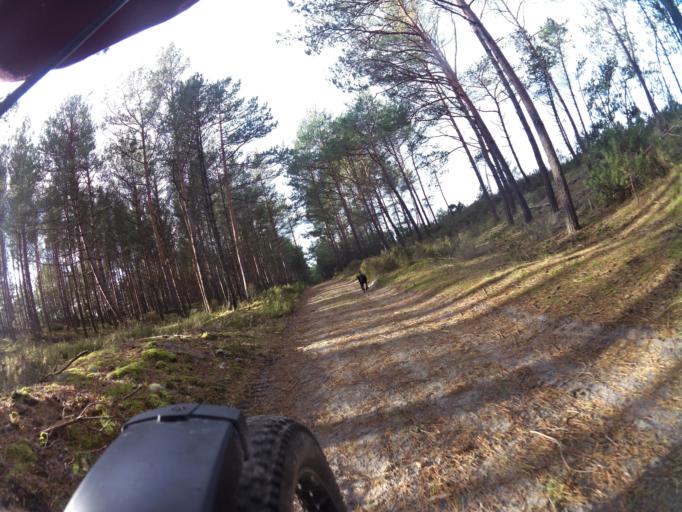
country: PL
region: Pomeranian Voivodeship
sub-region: Powiat wejherowski
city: Choczewo
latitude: 54.8062
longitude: 17.8026
